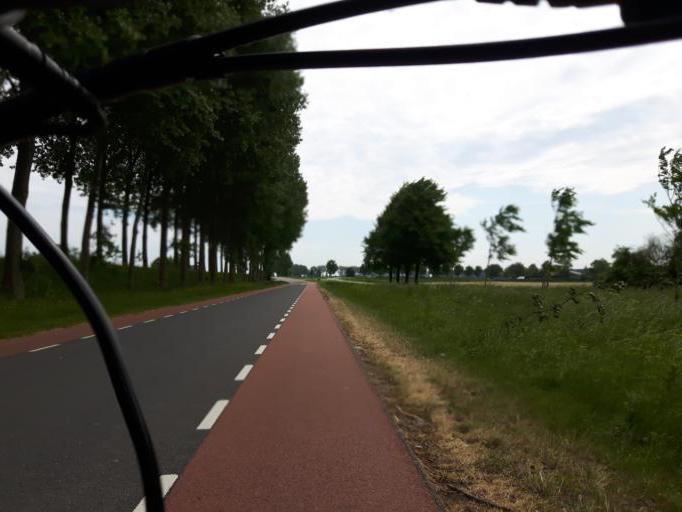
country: NL
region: Zeeland
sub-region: Gemeente Borsele
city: Borssele
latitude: 51.4409
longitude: 3.7840
